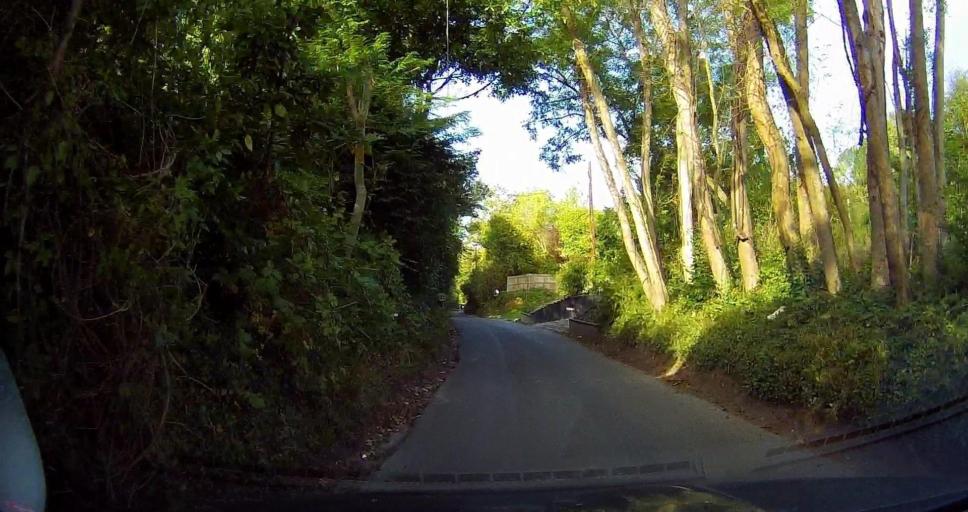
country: GB
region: England
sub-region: Kent
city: Longfield
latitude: 51.3586
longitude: 0.2894
